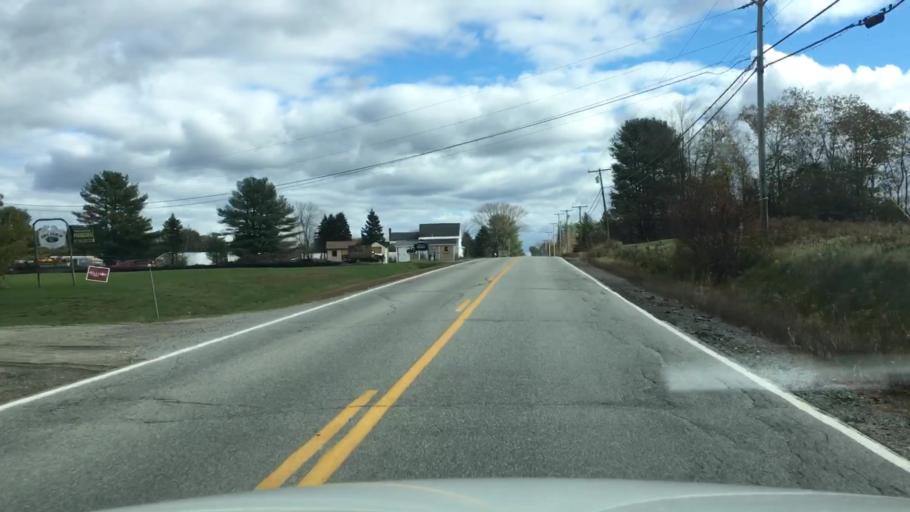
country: US
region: Maine
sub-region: Sagadahoc County
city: Richmond
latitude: 44.0950
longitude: -69.8436
